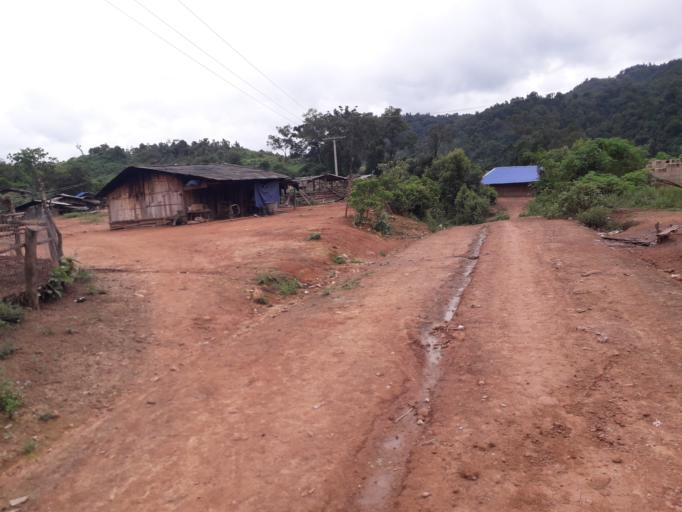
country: CN
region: Yunnan
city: Menglie
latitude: 22.2064
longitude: 101.6652
